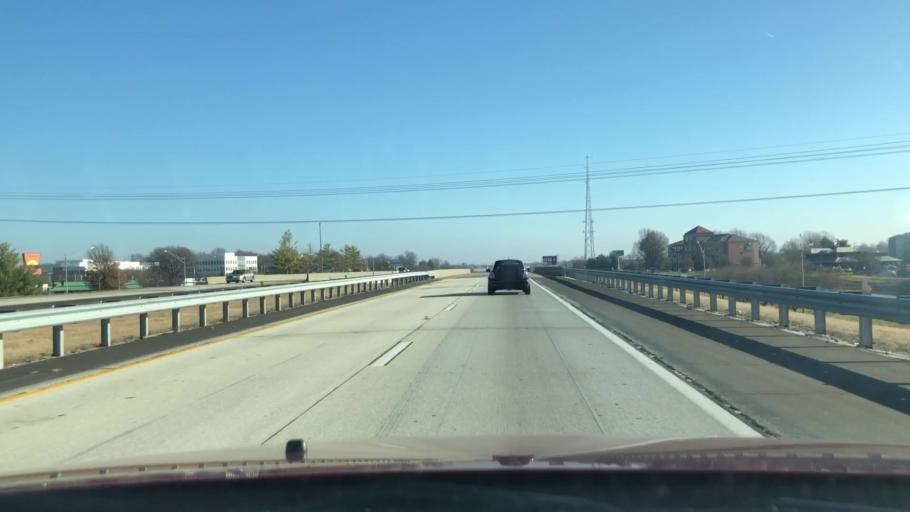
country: US
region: Missouri
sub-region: Greene County
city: Battlefield
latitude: 37.1358
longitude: -93.2975
